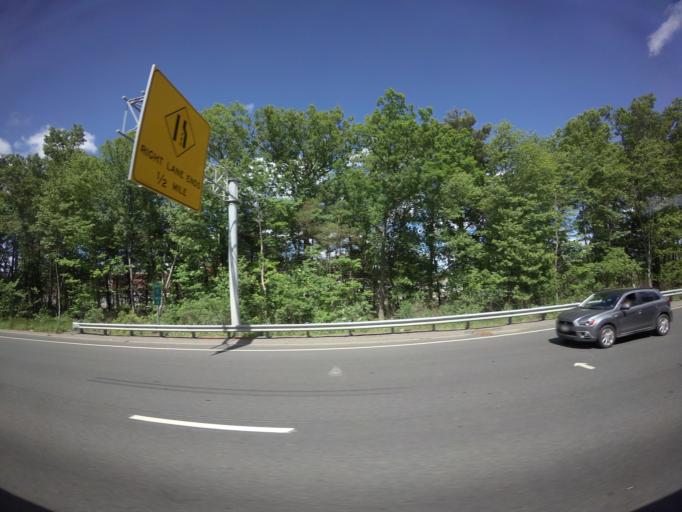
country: US
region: Massachusetts
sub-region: Middlesex County
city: Wilmington
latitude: 42.5886
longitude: -71.1616
